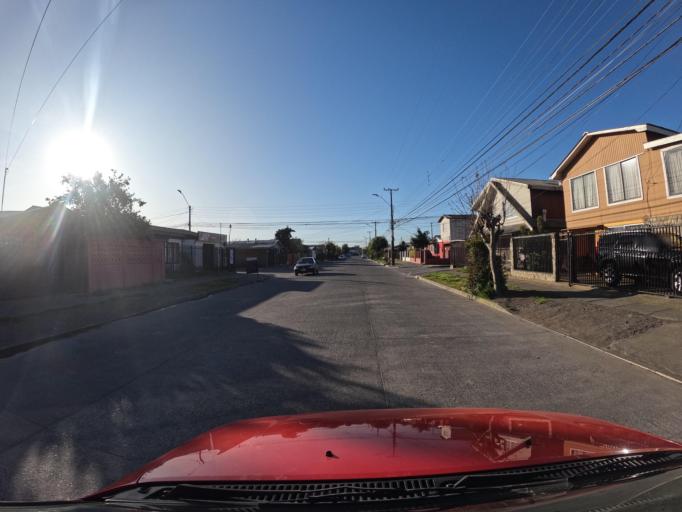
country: CL
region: Biobio
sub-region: Provincia de Concepcion
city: Chiguayante
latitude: -36.9284
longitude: -73.0270
